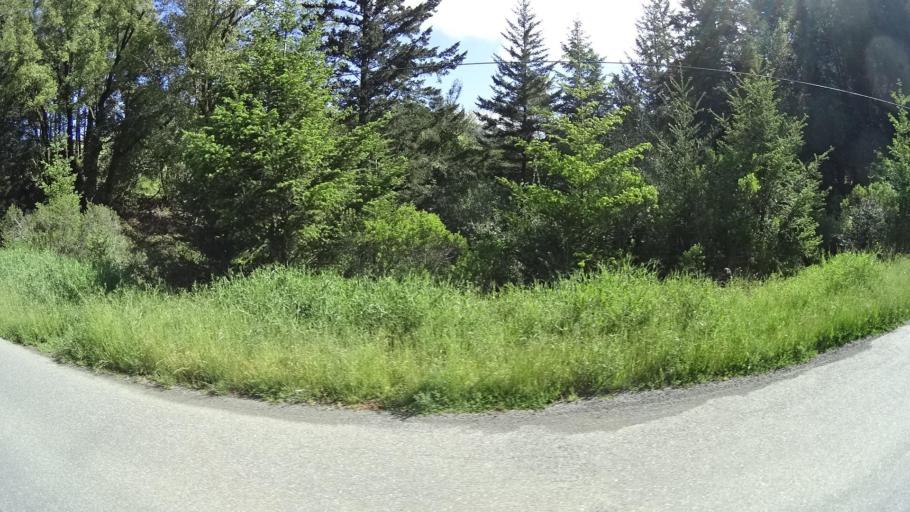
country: US
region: California
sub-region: Humboldt County
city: Ferndale
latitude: 40.3450
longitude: -124.3253
